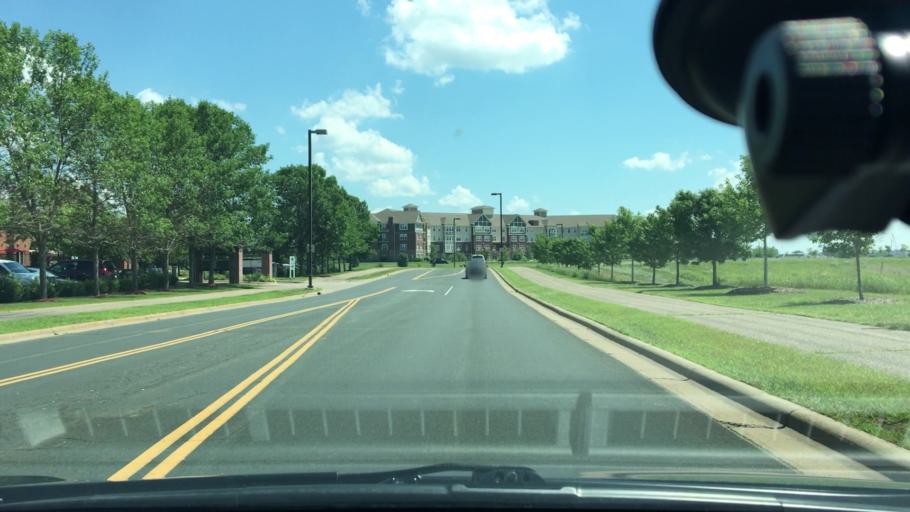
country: US
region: Minnesota
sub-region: Hennepin County
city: Maple Grove
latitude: 45.0983
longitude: -93.4374
